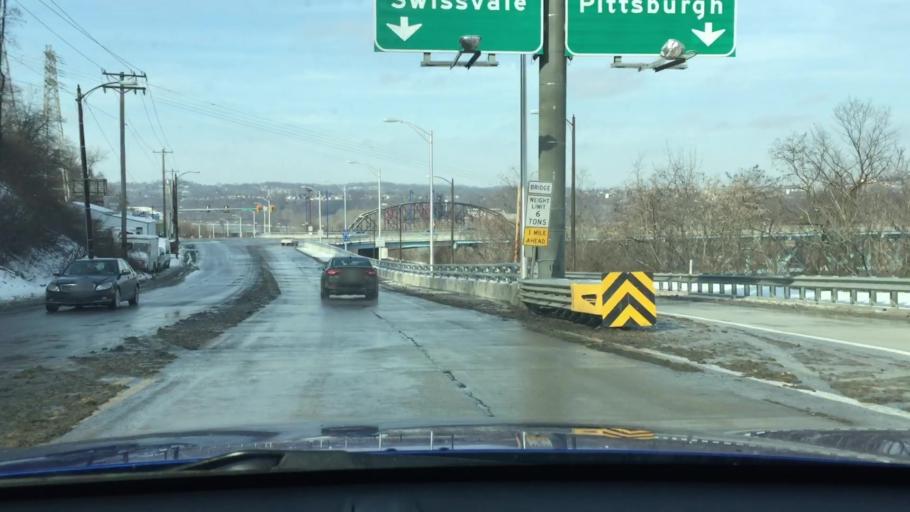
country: US
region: Pennsylvania
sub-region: Allegheny County
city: Whitaker
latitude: 40.4028
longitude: -79.8816
